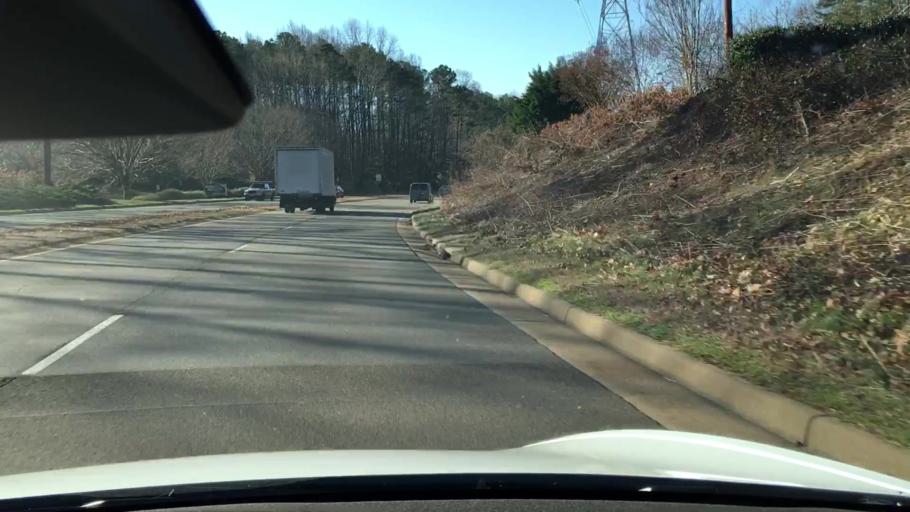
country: US
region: Virginia
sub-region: Henrico County
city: Tuckahoe
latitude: 37.5809
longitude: -77.5691
